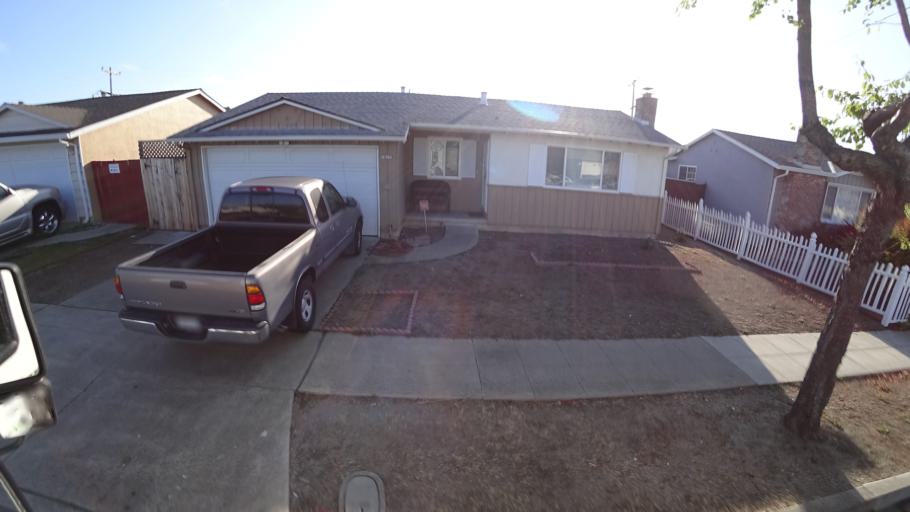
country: US
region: California
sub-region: Alameda County
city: Hayward
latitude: 37.6371
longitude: -122.0901
